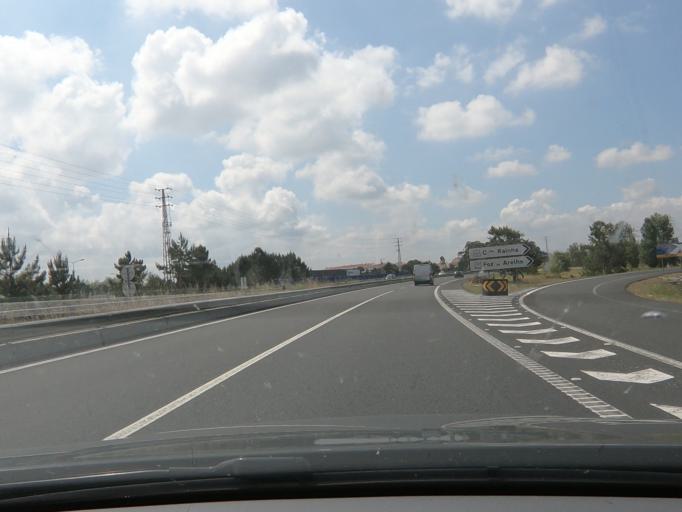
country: PT
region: Leiria
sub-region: Caldas da Rainha
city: Caldas da Rainha
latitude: 39.4092
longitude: -9.1548
